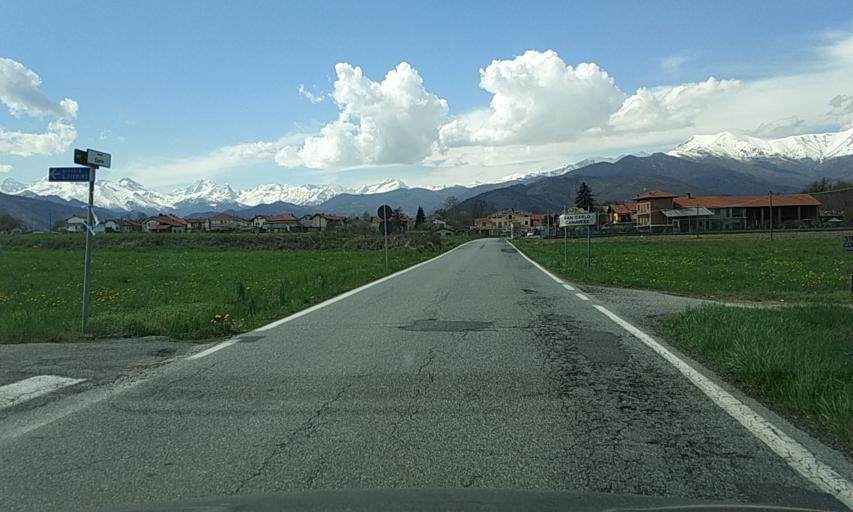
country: IT
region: Piedmont
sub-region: Provincia di Torino
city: Nole
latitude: 45.2548
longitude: 7.5867
